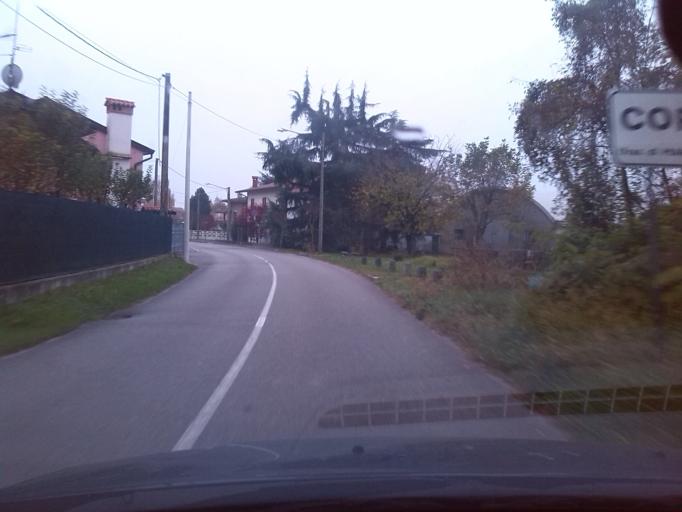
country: IT
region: Friuli Venezia Giulia
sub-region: Provincia di Gorizia
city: Moraro
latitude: 45.9253
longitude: 13.4809
